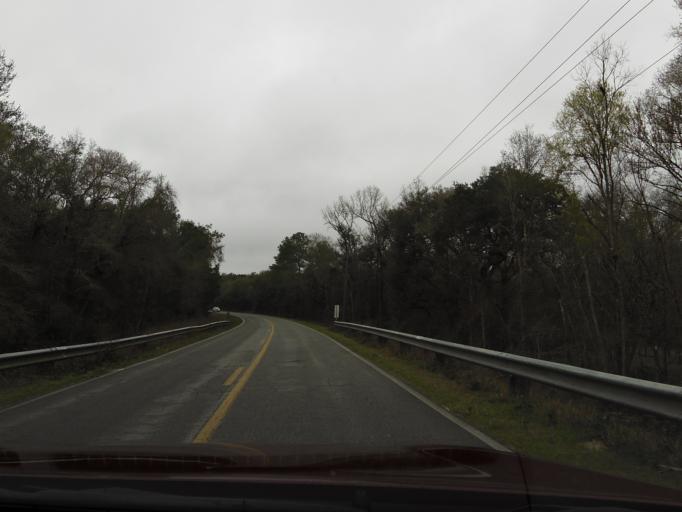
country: US
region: Florida
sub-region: Gilchrist County
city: Trenton
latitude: 29.8016
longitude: -82.9366
